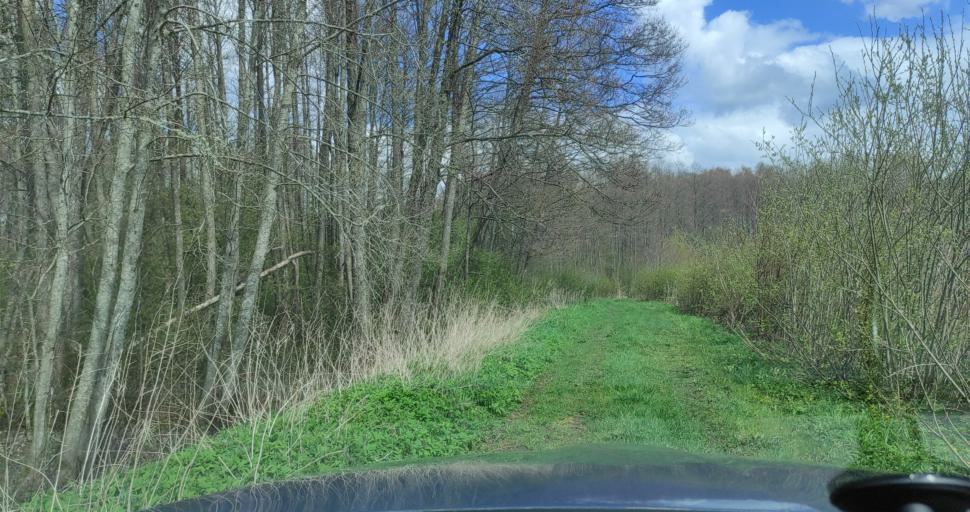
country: LV
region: Kuldigas Rajons
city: Kuldiga
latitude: 56.8713
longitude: 21.8296
